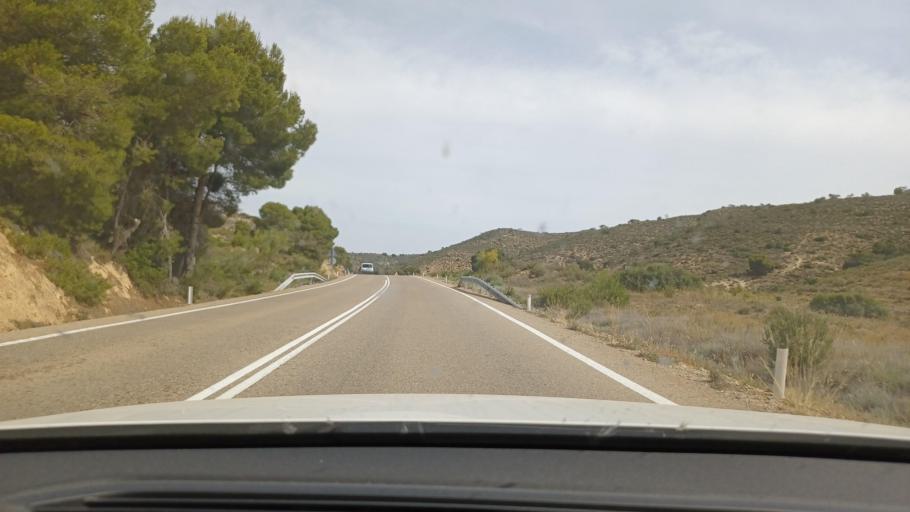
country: ES
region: Aragon
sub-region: Provincia de Zaragoza
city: Chiprana
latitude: 41.3485
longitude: -0.0919
